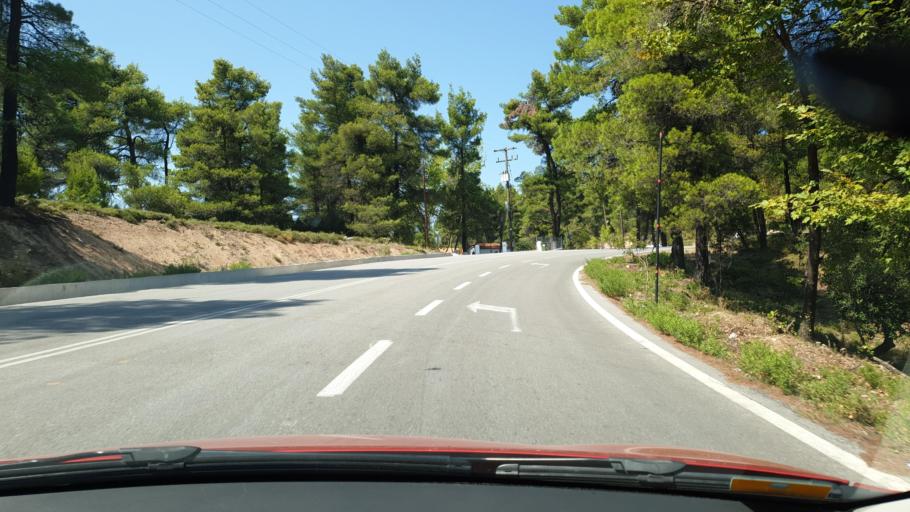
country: GR
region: Central Greece
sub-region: Nomos Evvoias
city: Politika
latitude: 38.6501
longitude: 23.5633
